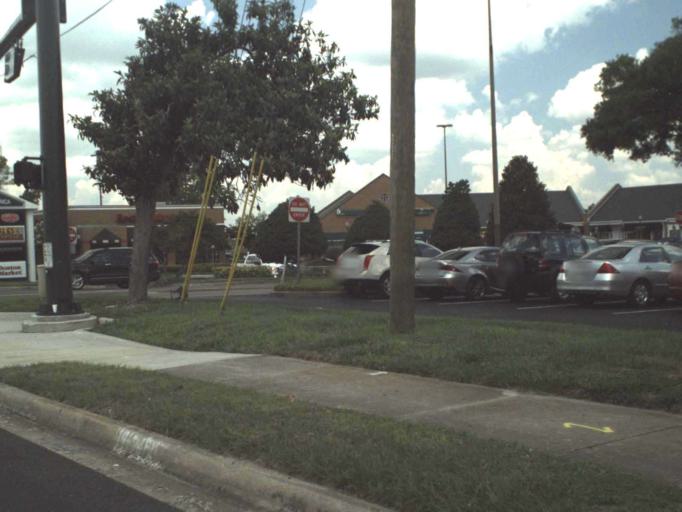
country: US
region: Florida
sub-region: Seminole County
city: Altamonte Springs
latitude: 28.6922
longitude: -81.3862
